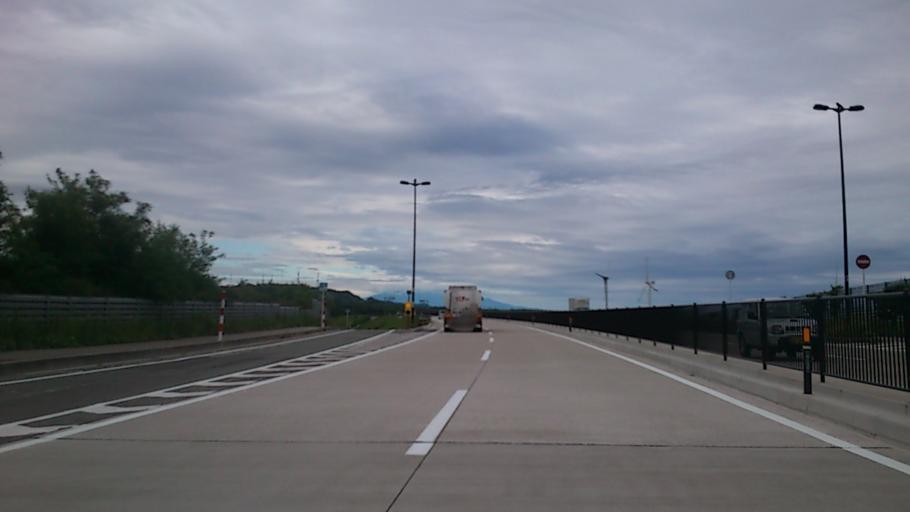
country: JP
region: Akita
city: Akita Shi
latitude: 39.7013
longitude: 140.0685
